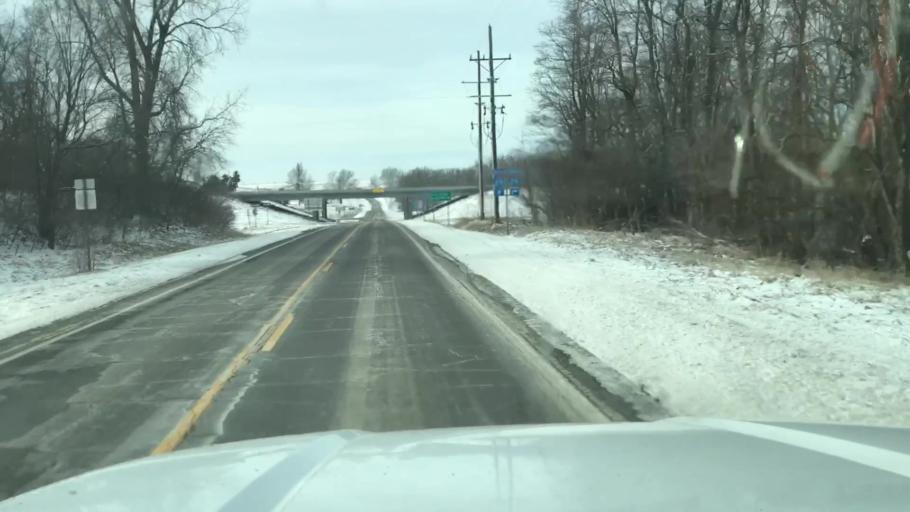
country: US
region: Missouri
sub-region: Holt County
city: Oregon
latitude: 40.0465
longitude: -95.1375
